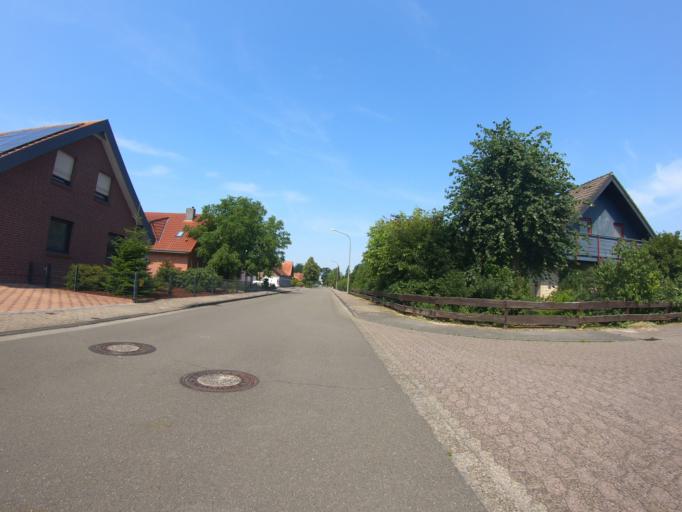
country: DE
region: Lower Saxony
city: Gifhorn
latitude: 52.4973
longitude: 10.5236
